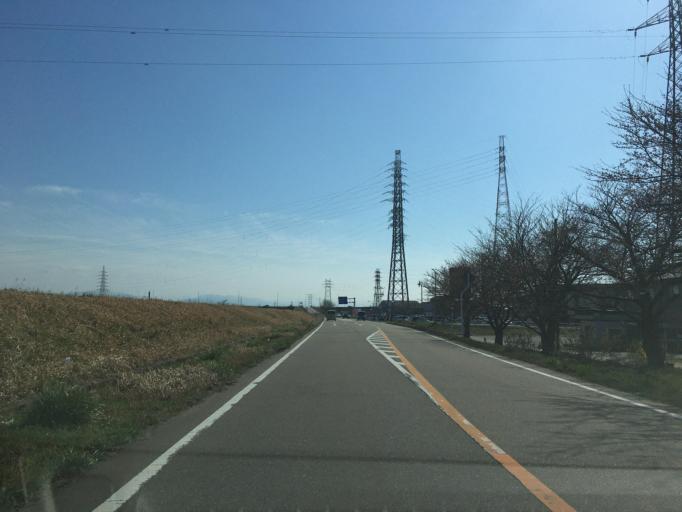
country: JP
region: Toyama
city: Nishishinminato
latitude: 36.7765
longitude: 137.0565
